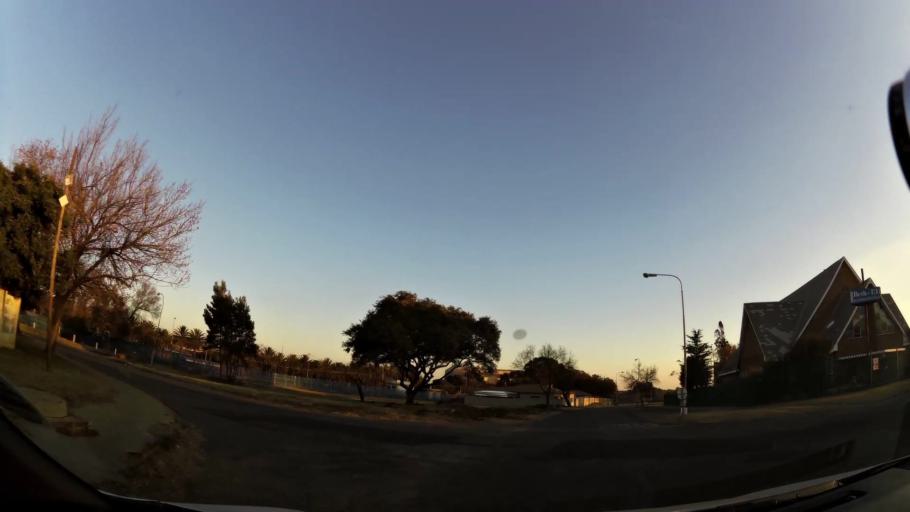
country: ZA
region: Gauteng
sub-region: Ekurhuleni Metropolitan Municipality
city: Germiston
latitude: -26.2702
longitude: 28.1616
